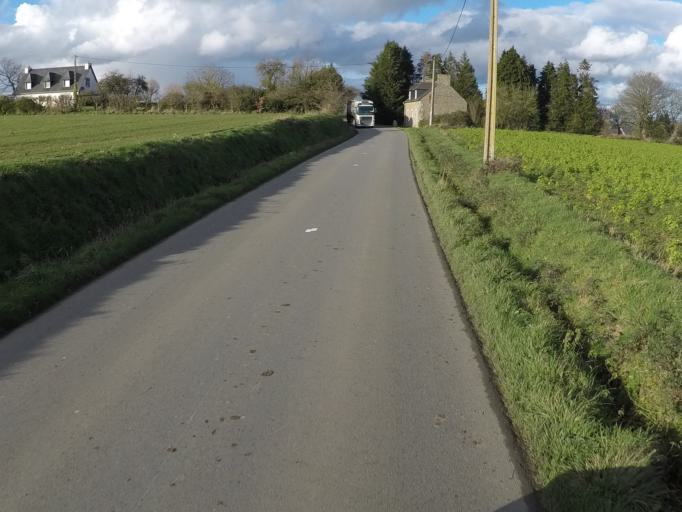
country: FR
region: Brittany
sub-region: Departement des Cotes-d'Armor
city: Plouagat
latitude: 48.5521
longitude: -2.9813
